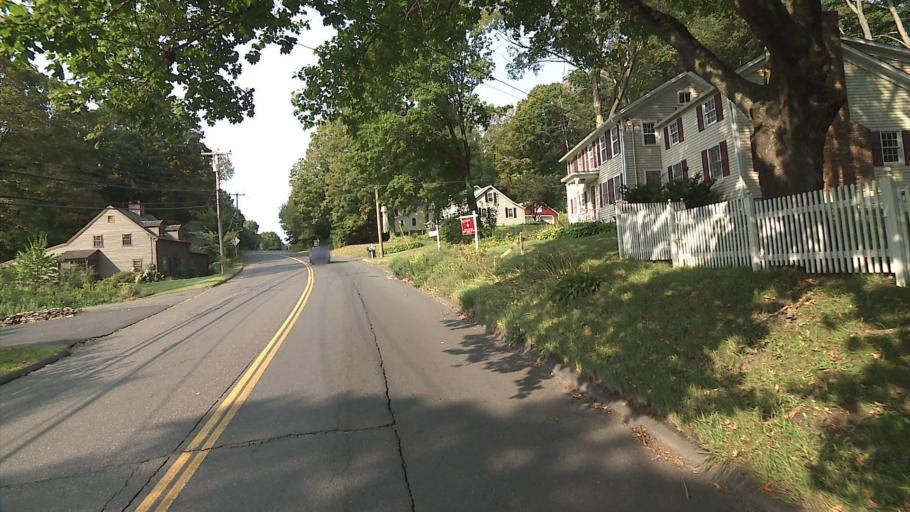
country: US
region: Connecticut
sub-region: Fairfield County
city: Newtown
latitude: 41.4196
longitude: -73.2867
